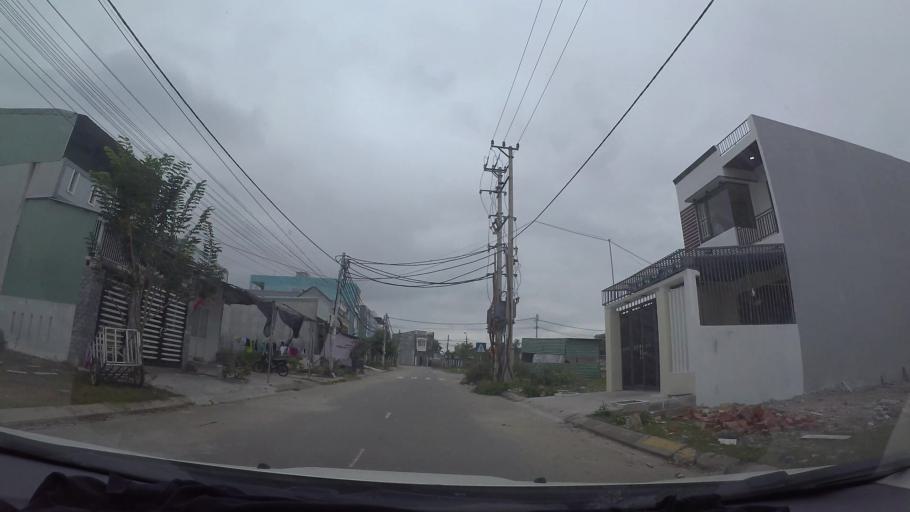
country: VN
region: Da Nang
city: Lien Chieu
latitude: 16.0699
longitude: 108.1403
